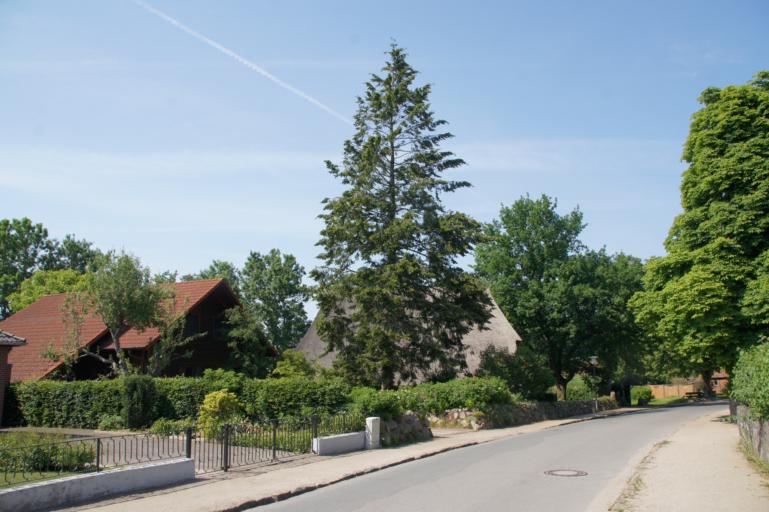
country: DE
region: Schleswig-Holstein
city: Bosdorf
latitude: 54.1714
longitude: 10.4940
